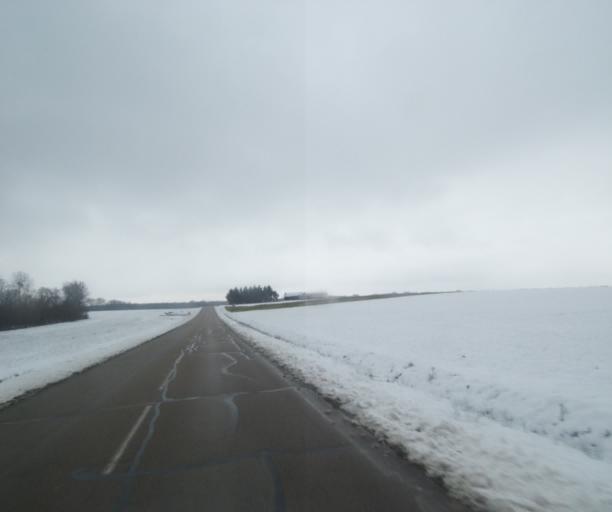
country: FR
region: Champagne-Ardenne
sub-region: Departement de la Haute-Marne
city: Laneuville-a-Remy
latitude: 48.4374
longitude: 4.8567
